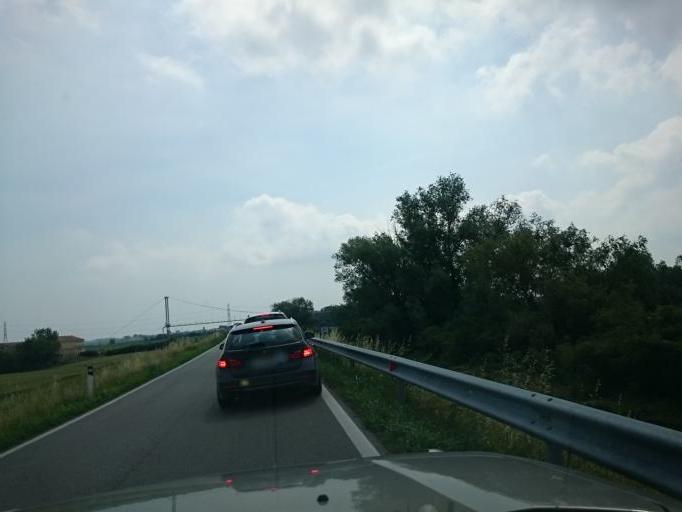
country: IT
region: Veneto
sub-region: Provincia di Padova
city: Codevigo
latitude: 45.2475
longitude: 12.1162
